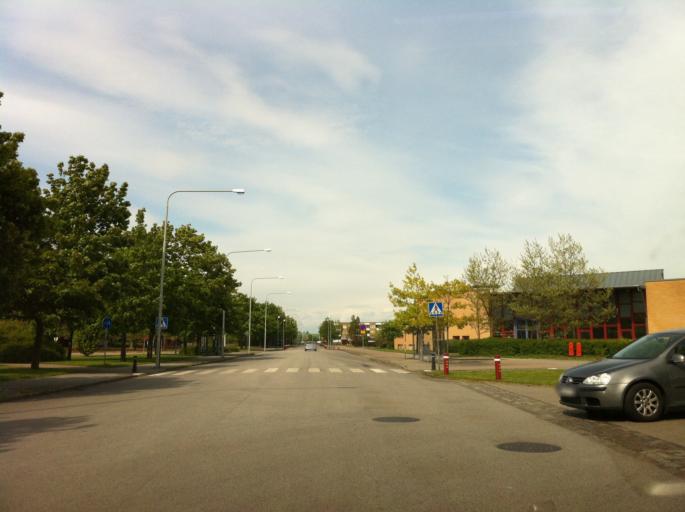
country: SE
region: Skane
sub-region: Landskrona
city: Landskrona
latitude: 55.8912
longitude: 12.8435
